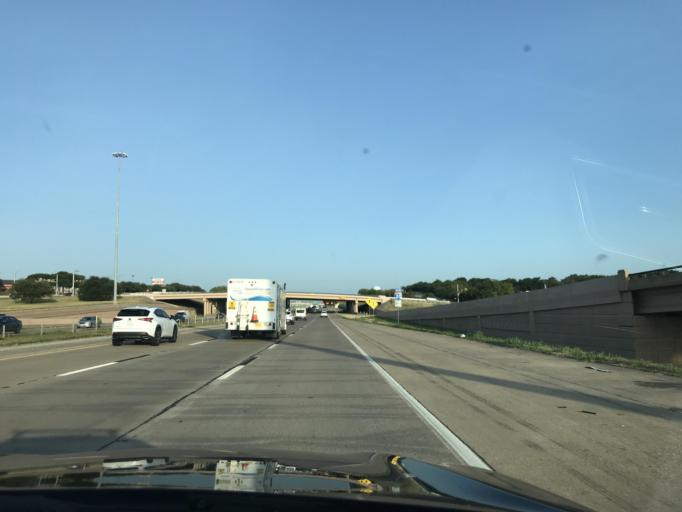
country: US
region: Texas
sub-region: Tarrant County
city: Benbrook
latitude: 32.6836
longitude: -97.4111
